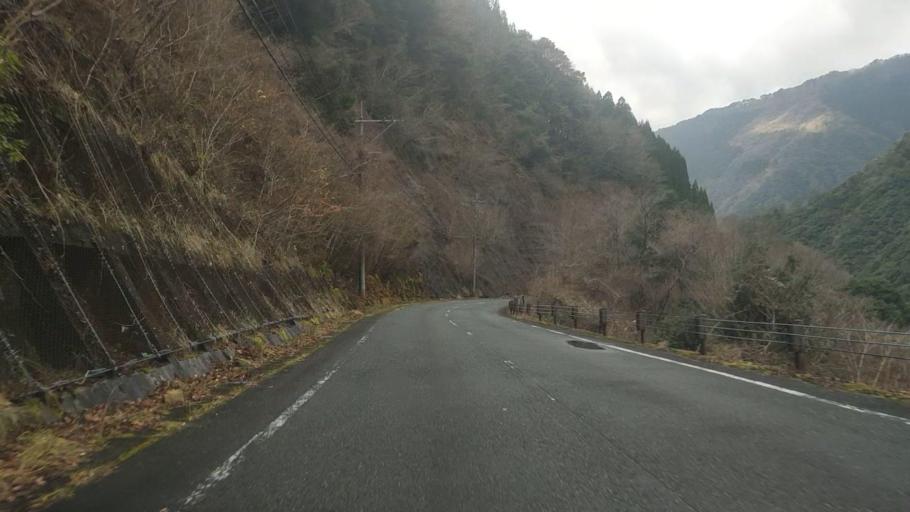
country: JP
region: Kumamoto
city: Matsubase
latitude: 32.5126
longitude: 130.9307
